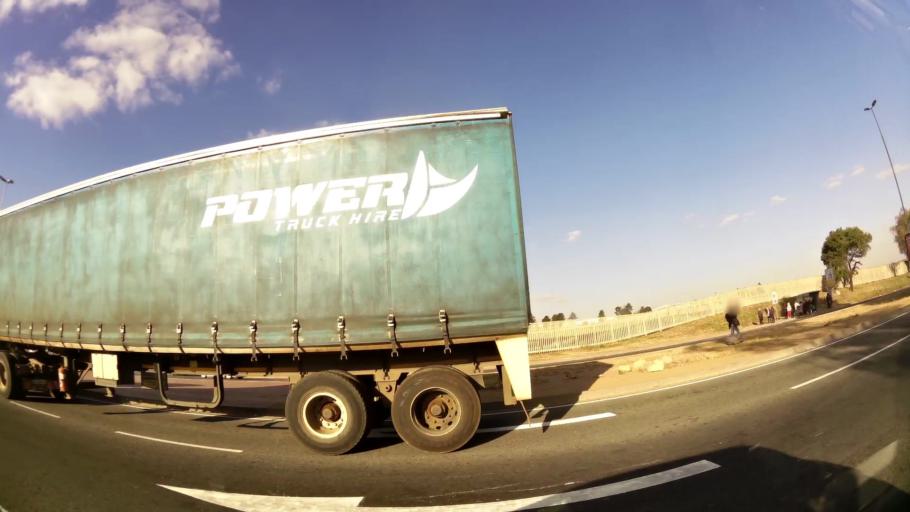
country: ZA
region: Gauteng
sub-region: City of Johannesburg Metropolitan Municipality
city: Midrand
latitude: -25.9824
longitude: 28.1328
